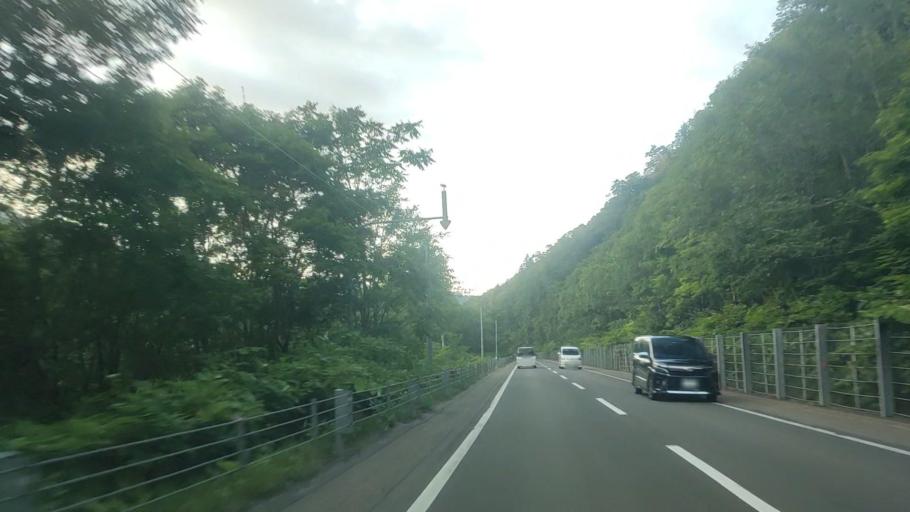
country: JP
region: Hokkaido
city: Ashibetsu
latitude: 43.3397
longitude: 142.1533
